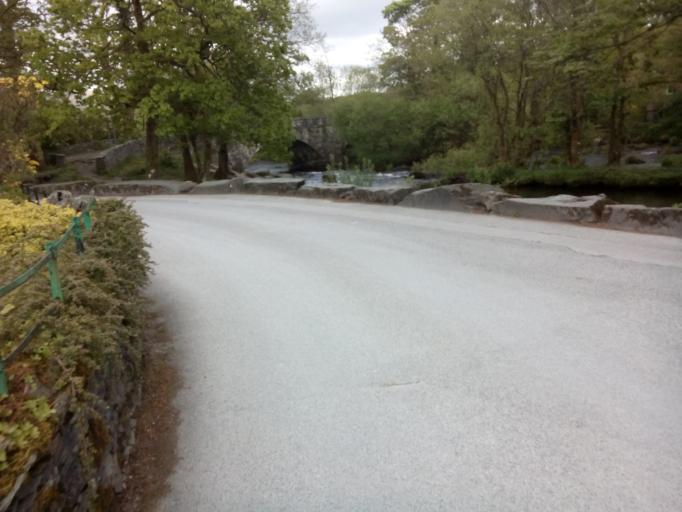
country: GB
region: England
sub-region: Cumbria
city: Ambleside
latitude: 54.4218
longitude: -3.0127
